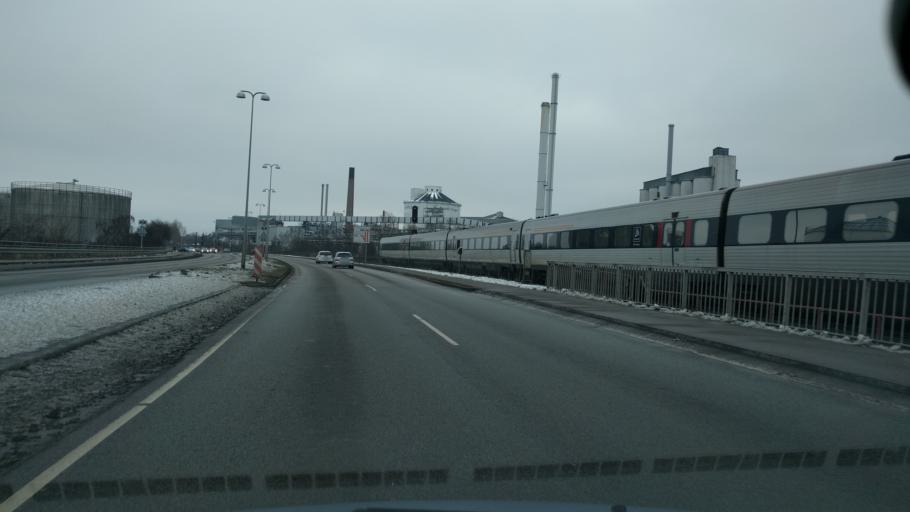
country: DK
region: Zealand
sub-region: Guldborgsund Kommune
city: Nykobing Falster
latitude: 54.7592
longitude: 11.8675
